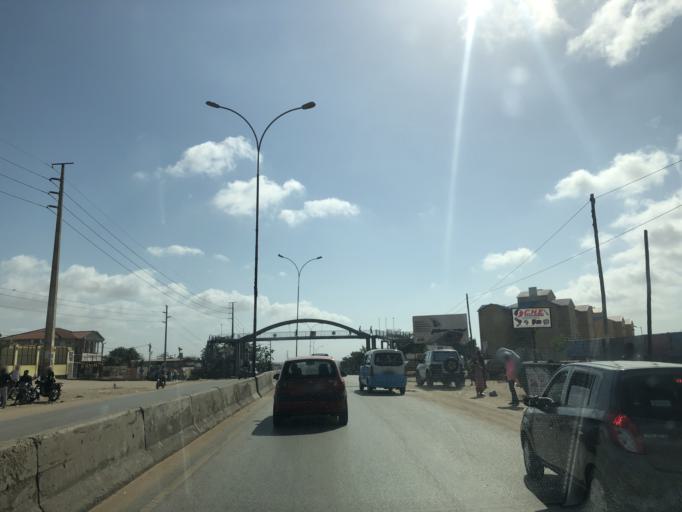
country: AO
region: Luanda
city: Luanda
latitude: -8.9081
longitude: 13.2414
